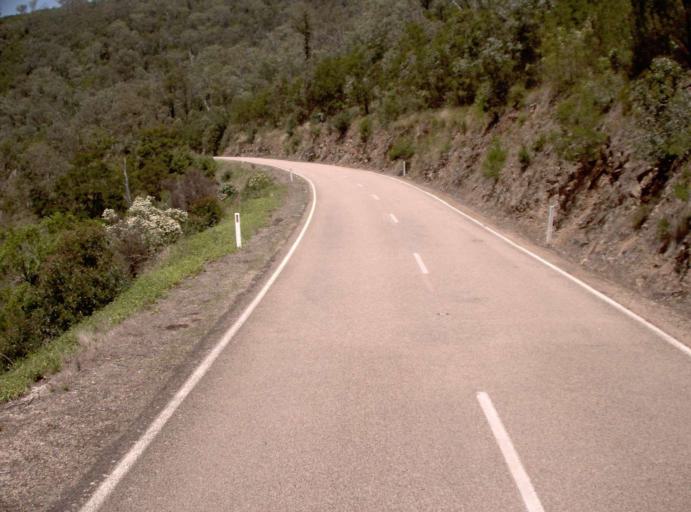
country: AU
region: Victoria
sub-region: East Gippsland
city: Lakes Entrance
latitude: -37.5323
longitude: 147.8536
